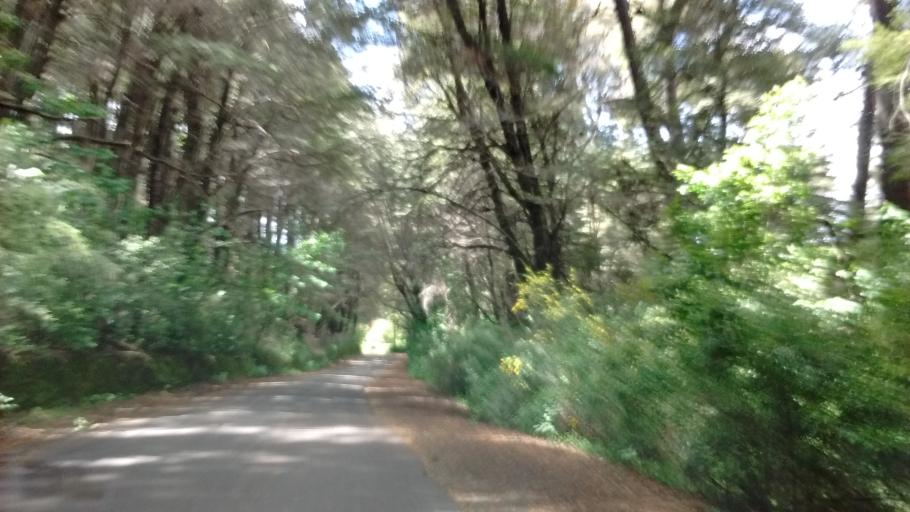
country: AR
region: Rio Negro
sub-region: Departamento de Bariloche
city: San Carlos de Bariloche
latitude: -41.0540
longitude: -71.5367
